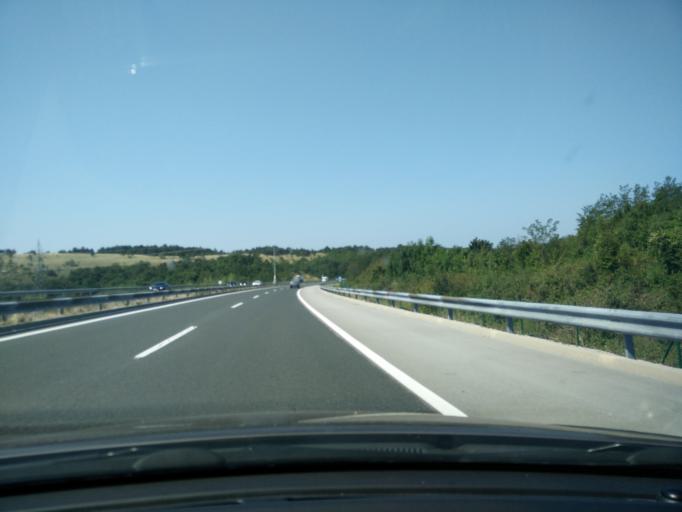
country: SI
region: Hrpelje-Kozina
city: Kozina
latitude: 45.5807
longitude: 13.9154
